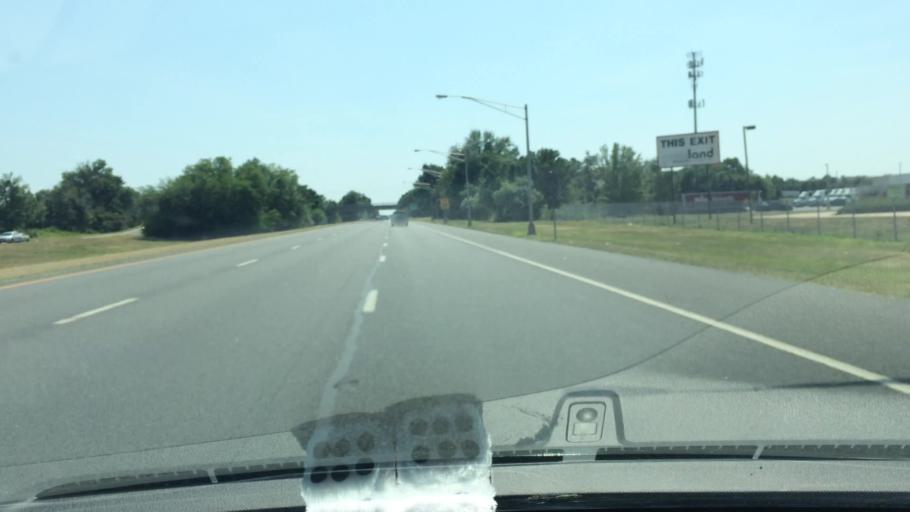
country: US
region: New Jersey
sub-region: Gloucester County
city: Beckett
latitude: 39.7647
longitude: -75.3576
